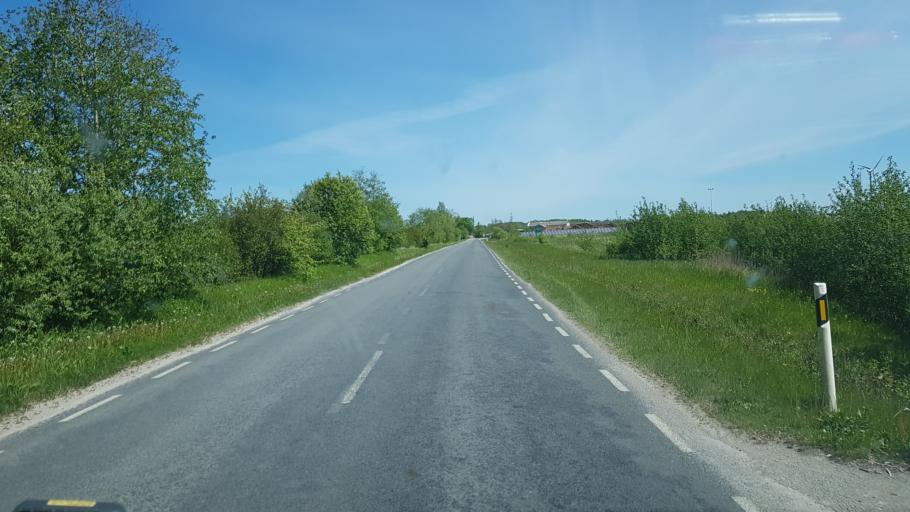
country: EE
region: Saare
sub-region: Kuressaare linn
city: Kuressaare
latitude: 58.2790
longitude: 22.5017
